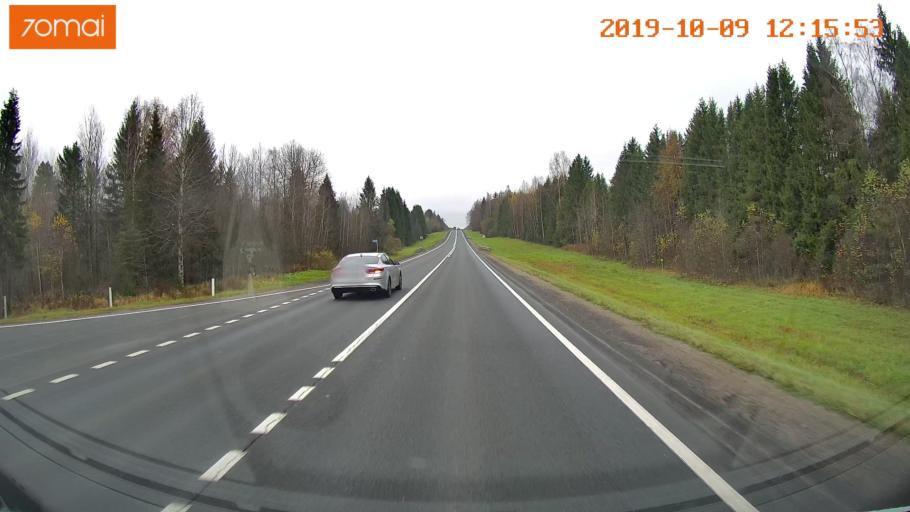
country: RU
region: Jaroslavl
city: Prechistoye
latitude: 58.4768
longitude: 40.3222
